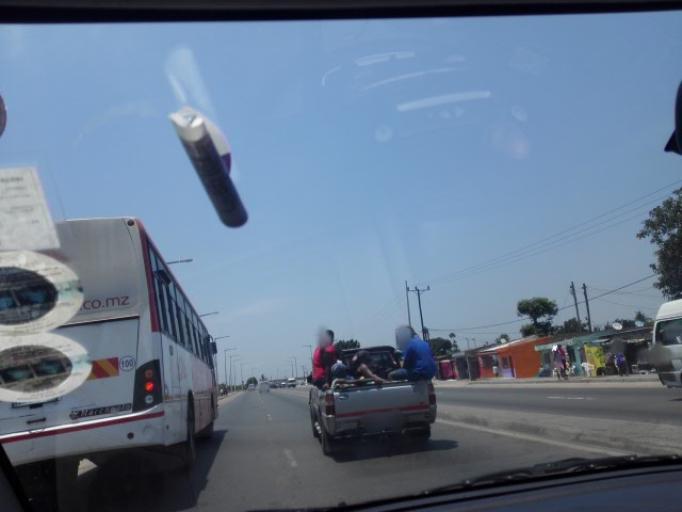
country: MZ
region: Maputo City
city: Maputo
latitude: -25.9152
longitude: 32.5653
